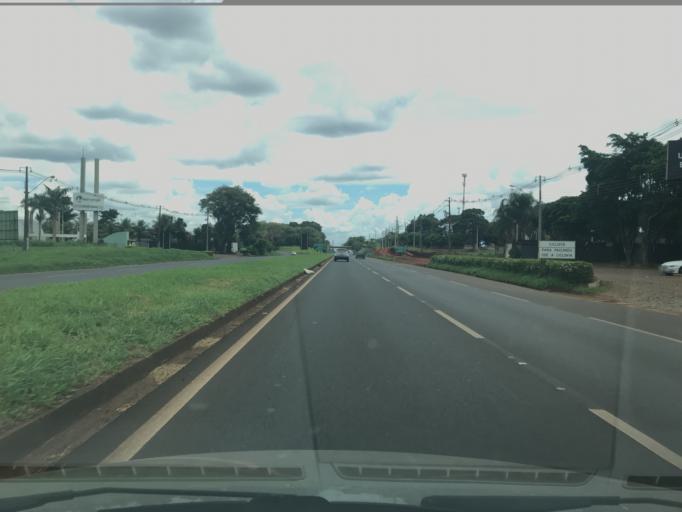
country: BR
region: Parana
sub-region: Maringa
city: Maringa
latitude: -23.4421
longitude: -51.9812
